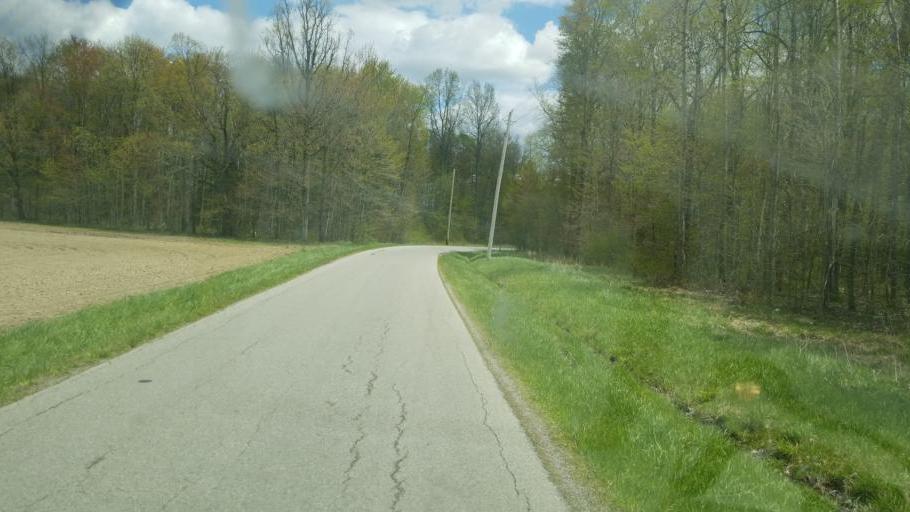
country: US
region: Ohio
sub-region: Crawford County
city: Galion
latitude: 40.7438
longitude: -82.8779
